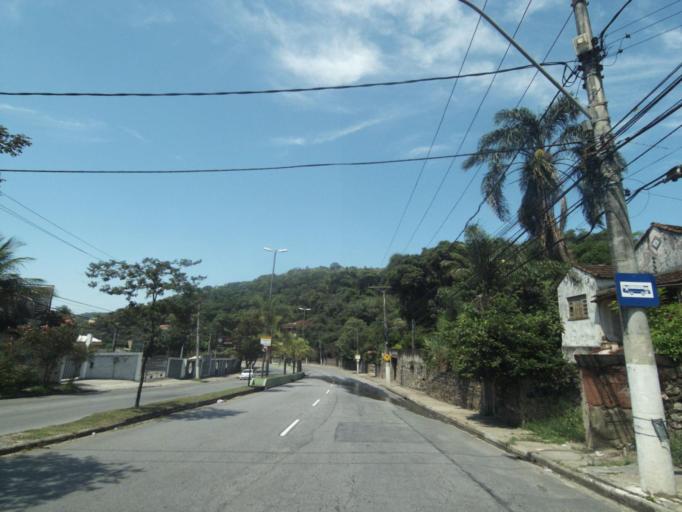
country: BR
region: Rio de Janeiro
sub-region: Niteroi
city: Niteroi
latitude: -22.9034
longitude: -43.0478
